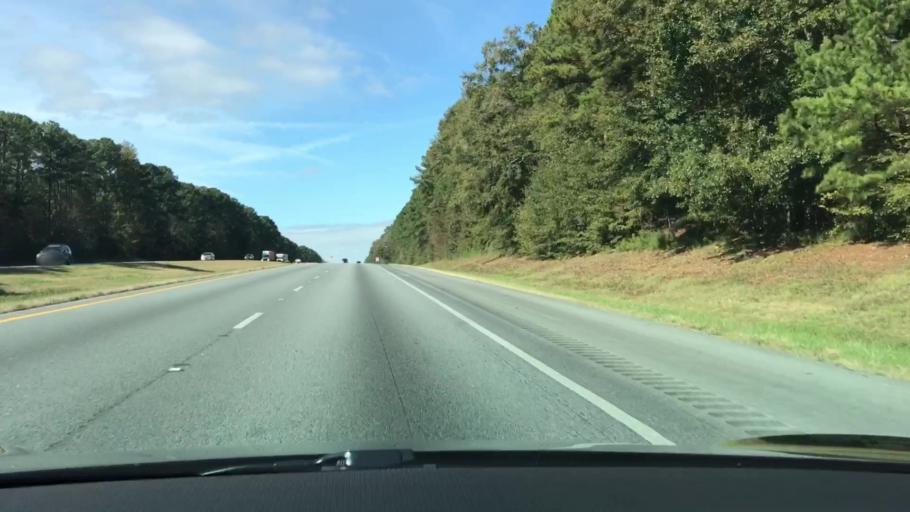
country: US
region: Georgia
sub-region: Morgan County
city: Madison
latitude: 33.5835
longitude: -83.5971
